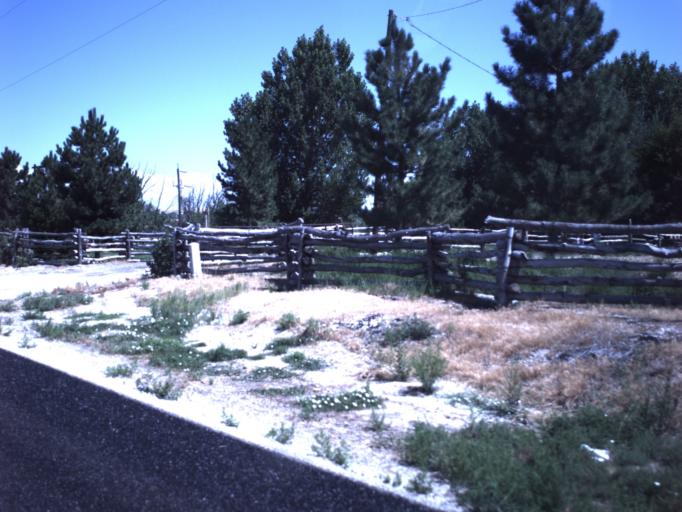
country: US
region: Utah
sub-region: Emery County
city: Ferron
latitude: 39.0723
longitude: -111.1315
